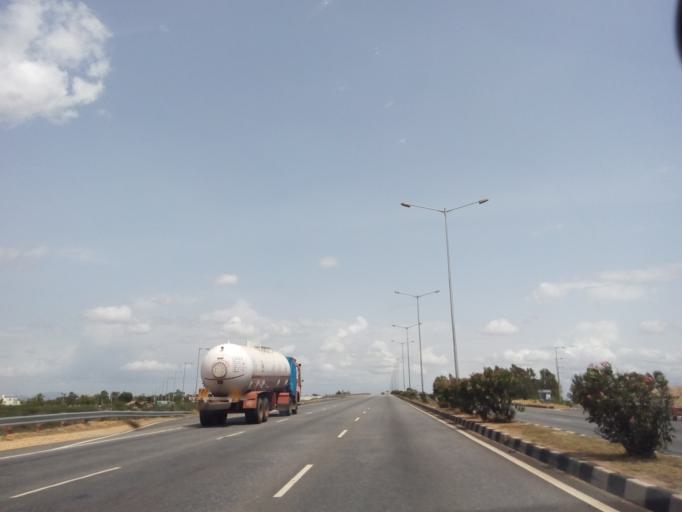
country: IN
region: Karnataka
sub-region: Tumkur
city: Sira
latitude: 13.7391
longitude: 76.8908
